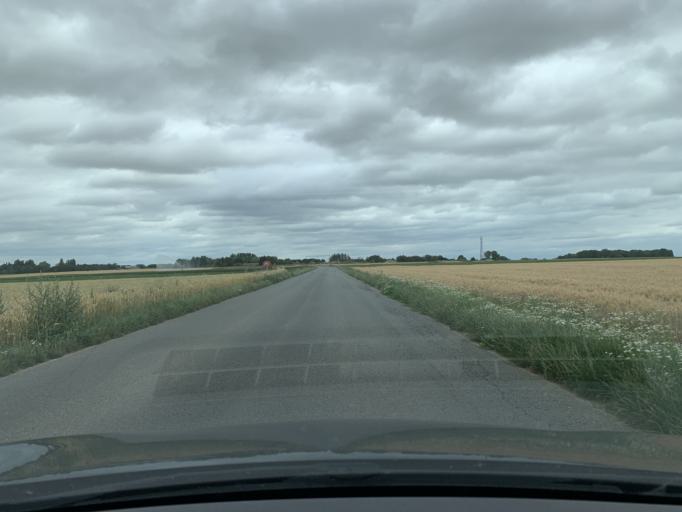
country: FR
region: Nord-Pas-de-Calais
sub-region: Departement du Nord
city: Raillencourt-Sainte-Olle
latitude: 50.2022
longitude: 3.1414
